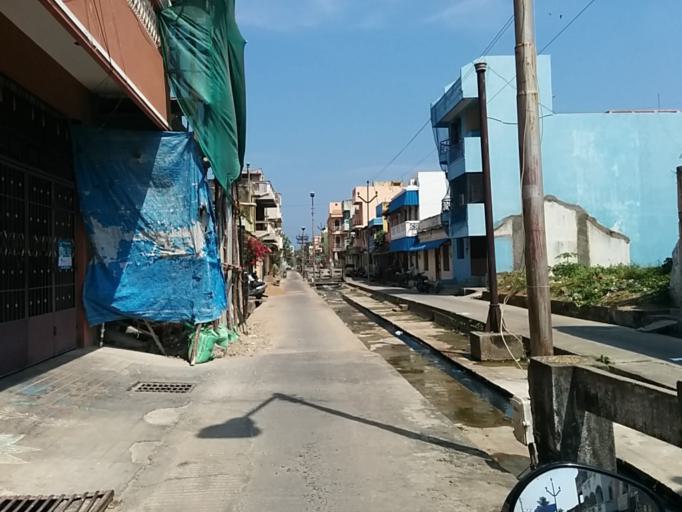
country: IN
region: Pondicherry
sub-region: Puducherry
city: Puducherry
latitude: 11.9323
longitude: 79.8273
